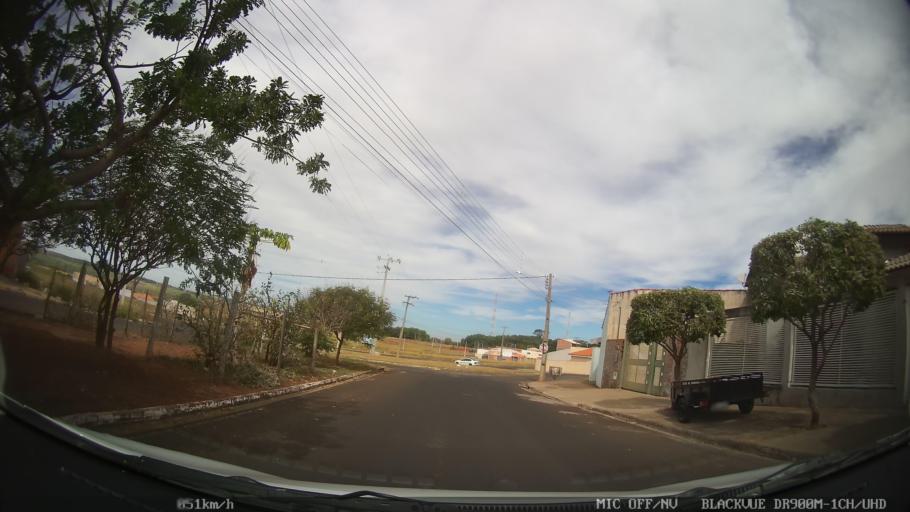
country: BR
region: Sao Paulo
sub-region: Catanduva
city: Catanduva
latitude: -21.1693
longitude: -48.9694
